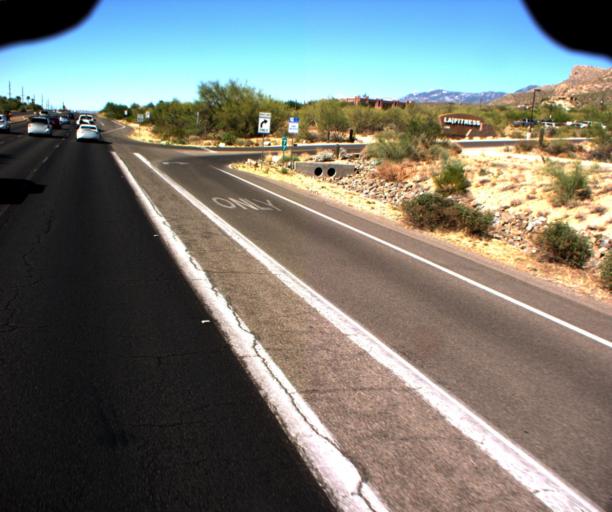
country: US
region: Arizona
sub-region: Pima County
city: Oro Valley
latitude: 32.3670
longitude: -110.9691
